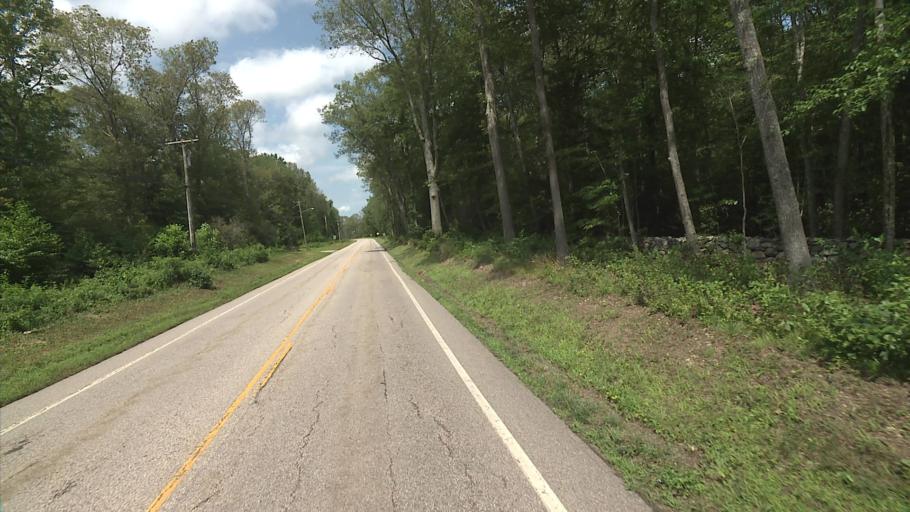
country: US
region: Connecticut
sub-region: New London County
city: Montville Center
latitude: 41.4200
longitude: -72.2143
